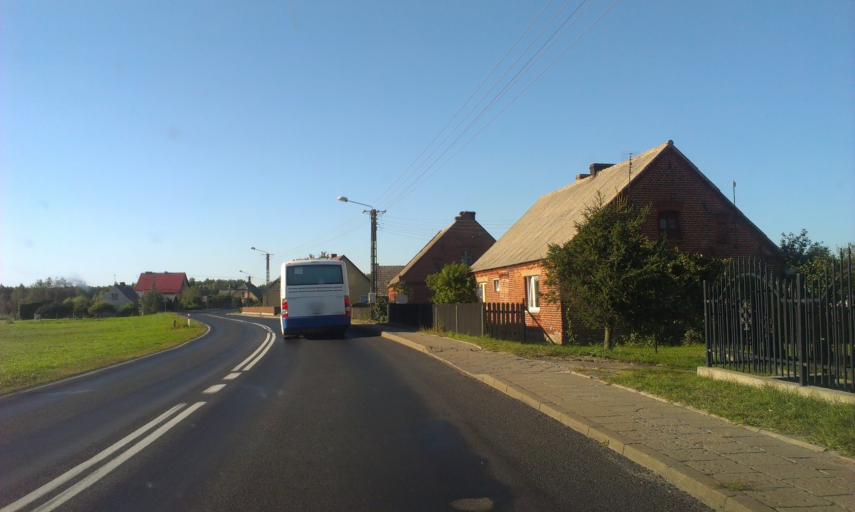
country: PL
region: Kujawsko-Pomorskie
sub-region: Powiat tucholski
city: Cekcyn
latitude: 53.5330
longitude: 17.9442
